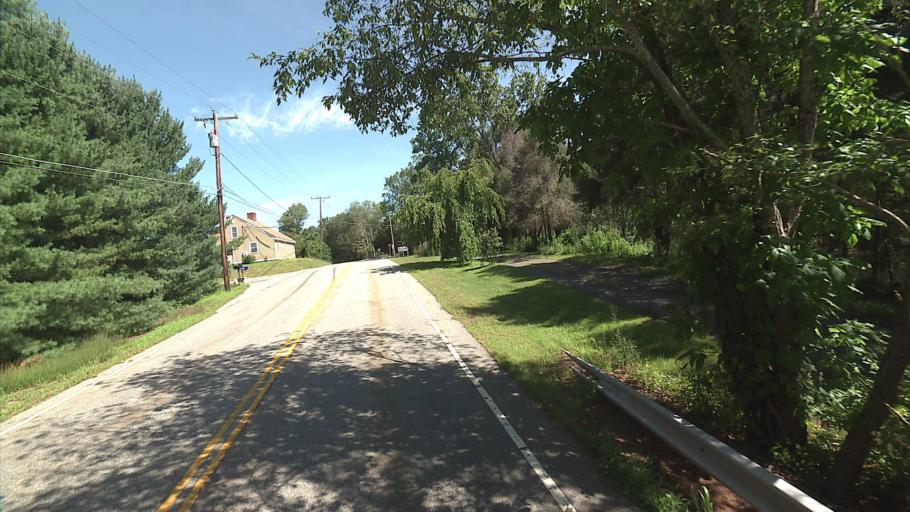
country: US
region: Connecticut
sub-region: New London County
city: Baltic
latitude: 41.6769
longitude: -72.0842
